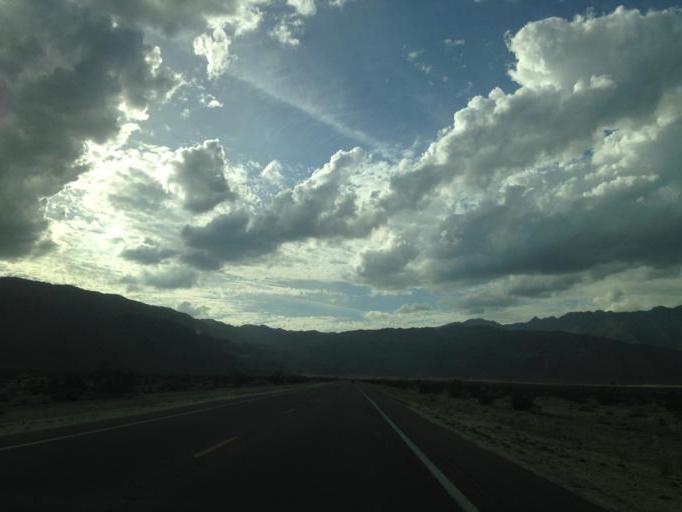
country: US
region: California
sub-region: San Diego County
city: Borrego Springs
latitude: 33.2115
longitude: -116.3574
